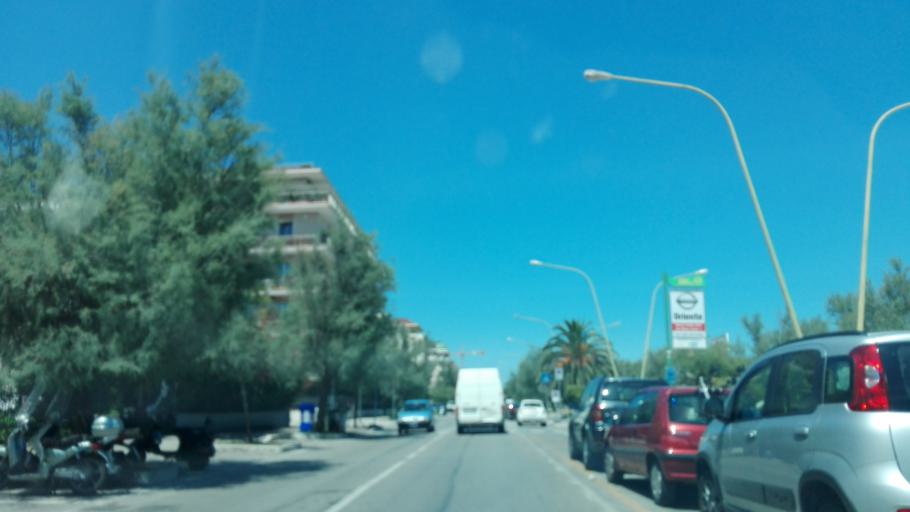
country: IT
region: Abruzzo
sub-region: Provincia di Pescara
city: Pescara
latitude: 42.4783
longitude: 14.2042
